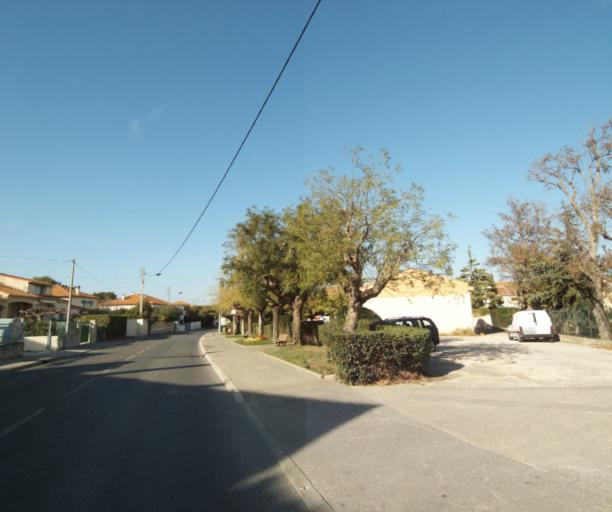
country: FR
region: Provence-Alpes-Cote d'Azur
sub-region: Departement des Bouches-du-Rhone
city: Chateauneuf-les-Martigues
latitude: 43.3838
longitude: 5.1604
